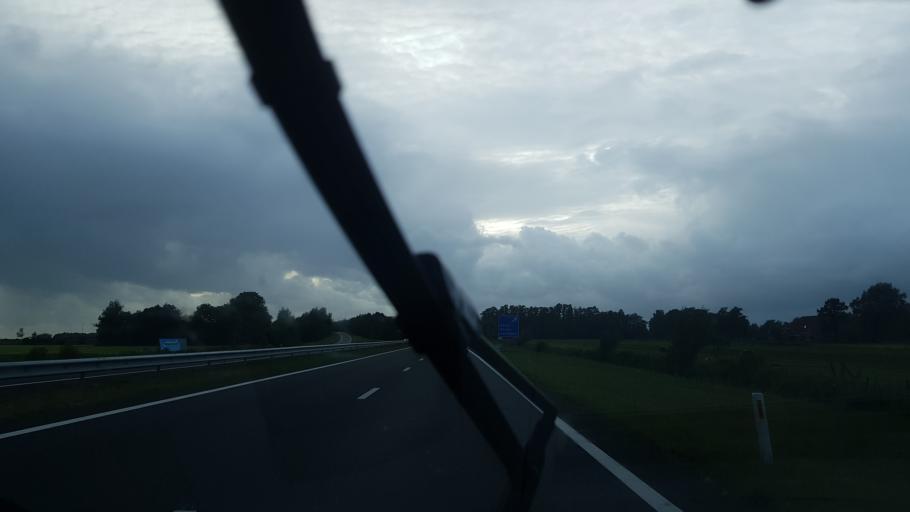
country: NL
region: Friesland
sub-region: Gemeente Tytsjerksteradiel
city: Garyp
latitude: 53.1589
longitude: 5.9577
